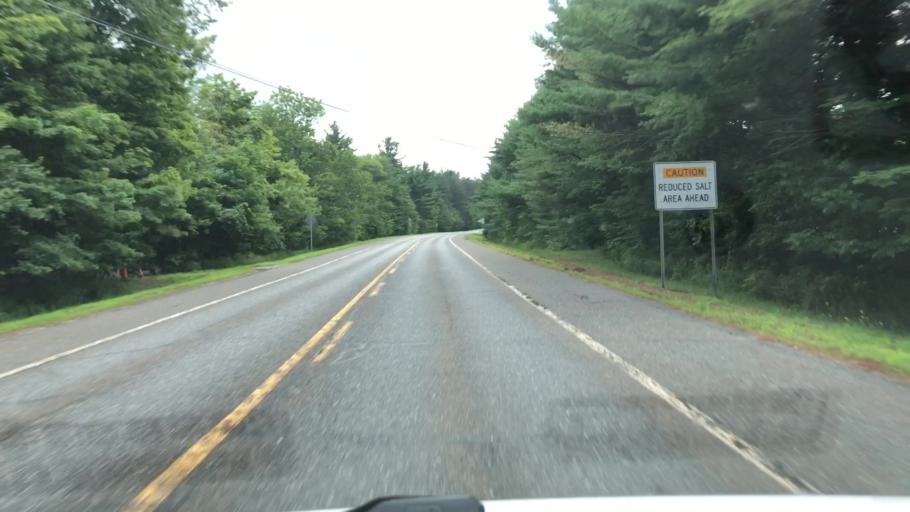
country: US
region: Massachusetts
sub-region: Franklin County
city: Ashfield
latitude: 42.4602
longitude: -72.8054
